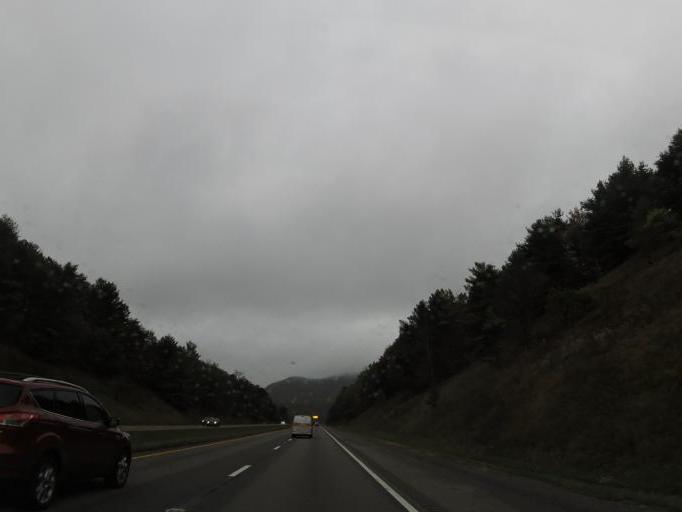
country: US
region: Virginia
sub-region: Wythe County
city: Wytheville
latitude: 37.0122
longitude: -81.1050
